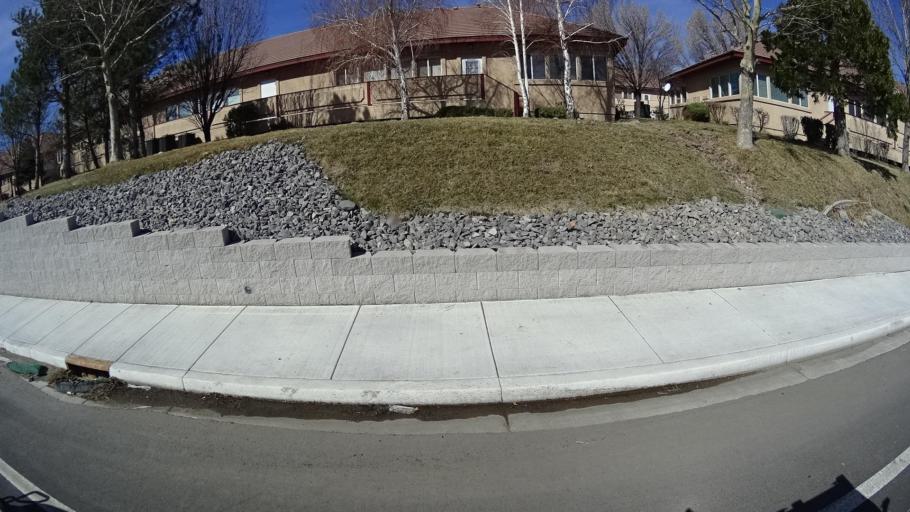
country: US
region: Nevada
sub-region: Washoe County
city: Sparks
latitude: 39.5584
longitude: -119.7723
